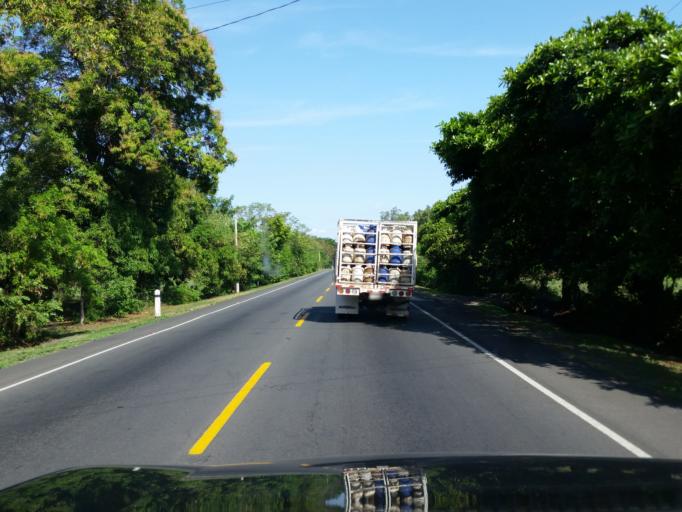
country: NI
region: Leon
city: Leon
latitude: 12.3951
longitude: -86.8493
